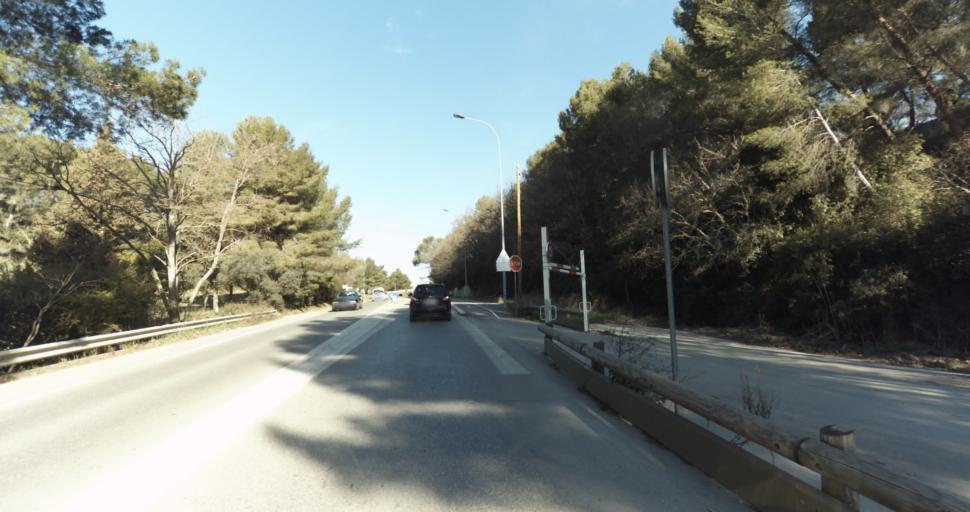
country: FR
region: Provence-Alpes-Cote d'Azur
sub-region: Departement des Bouches-du-Rhone
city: Aix-en-Provence
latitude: 43.5515
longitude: 5.4372
